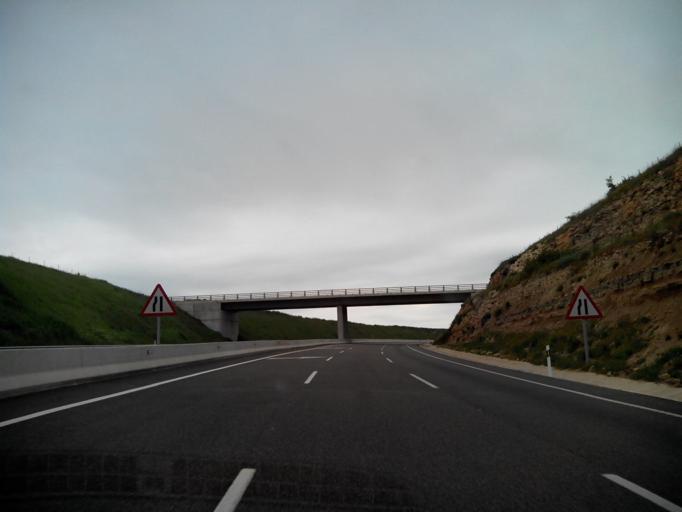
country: ES
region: Catalonia
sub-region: Provincia de Barcelona
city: Pujalt
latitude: 41.7347
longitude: 1.4371
